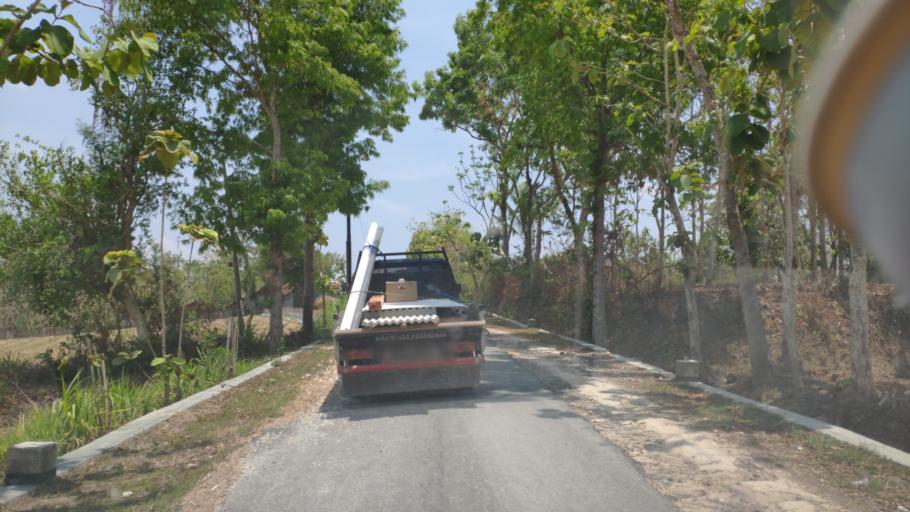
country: ID
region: Central Java
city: Talok
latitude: -7.0391
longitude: 111.3011
